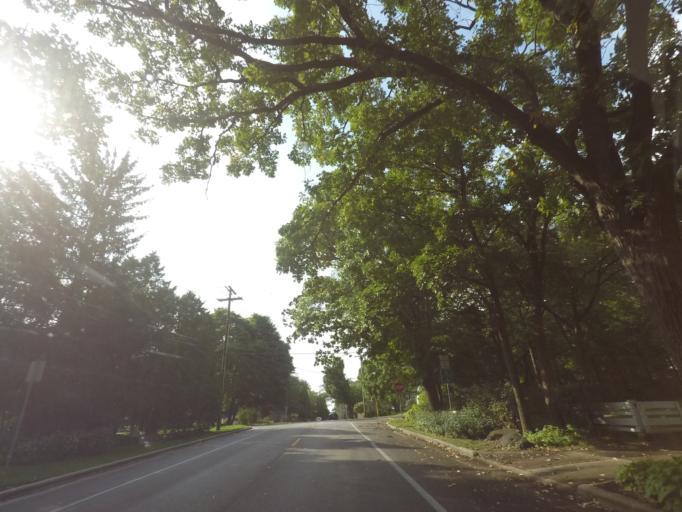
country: US
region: Wisconsin
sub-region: Dane County
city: Shorewood Hills
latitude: 43.0396
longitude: -89.4735
